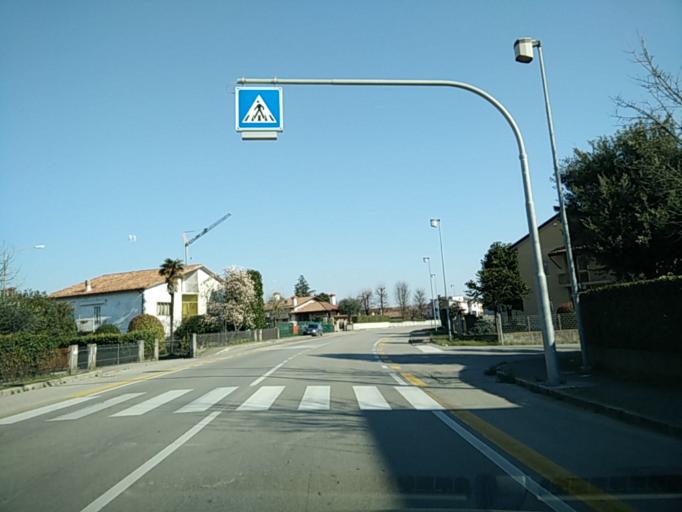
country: IT
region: Friuli Venezia Giulia
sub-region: Provincia di Pordenone
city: San Vito al Tagliamento
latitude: 45.9131
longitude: 12.8468
